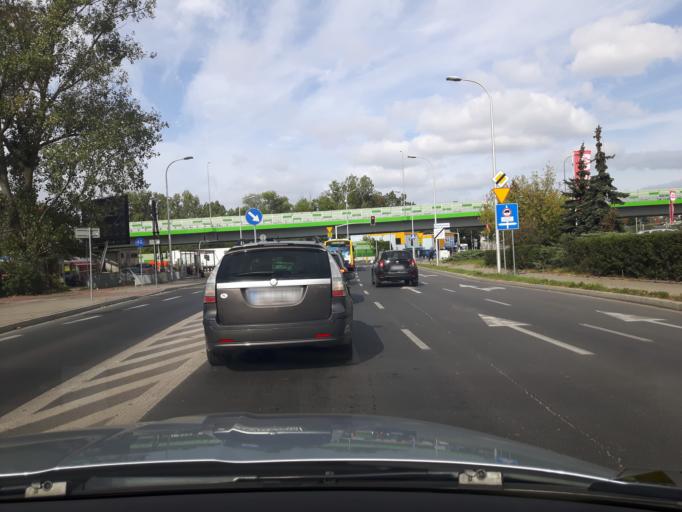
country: PL
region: Masovian Voivodeship
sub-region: Warszawa
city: Rembertow
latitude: 52.2411
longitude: 21.1368
